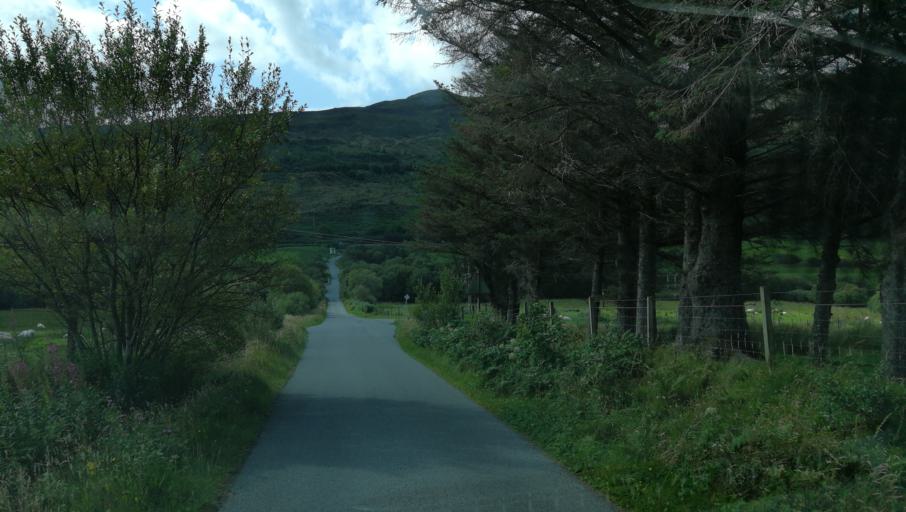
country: GB
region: Scotland
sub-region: Highland
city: Portree
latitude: 57.3873
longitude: -6.1960
